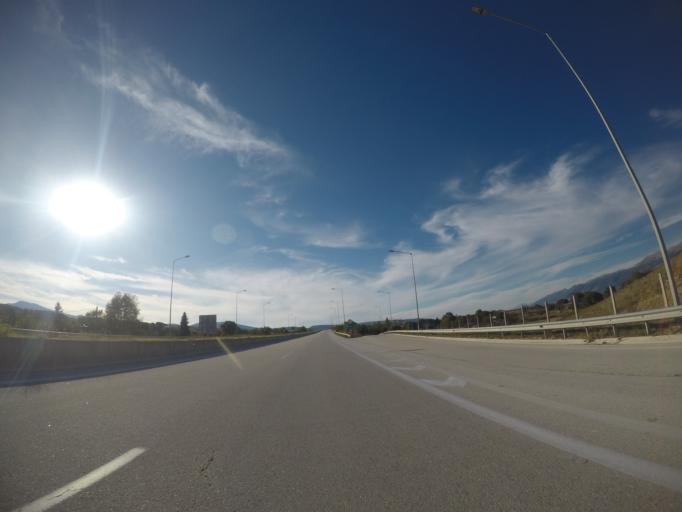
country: GR
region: Epirus
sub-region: Nomos Ioanninon
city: Koutselio
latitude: 39.5982
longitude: 20.9142
